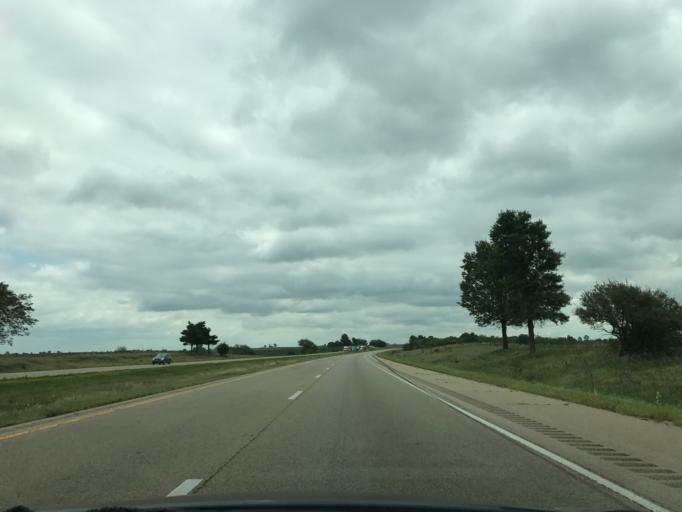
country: US
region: Illinois
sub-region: Bureau County
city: Depue
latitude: 41.3997
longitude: -89.3128
